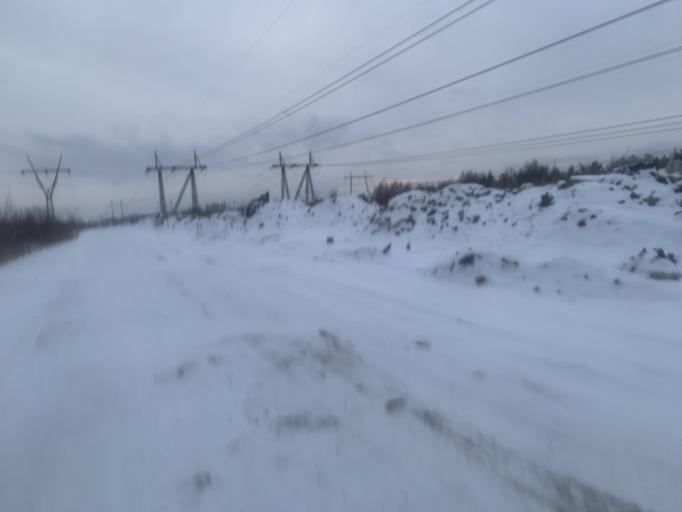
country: RU
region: Chelyabinsk
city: Roshchino
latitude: 55.1935
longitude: 61.2599
